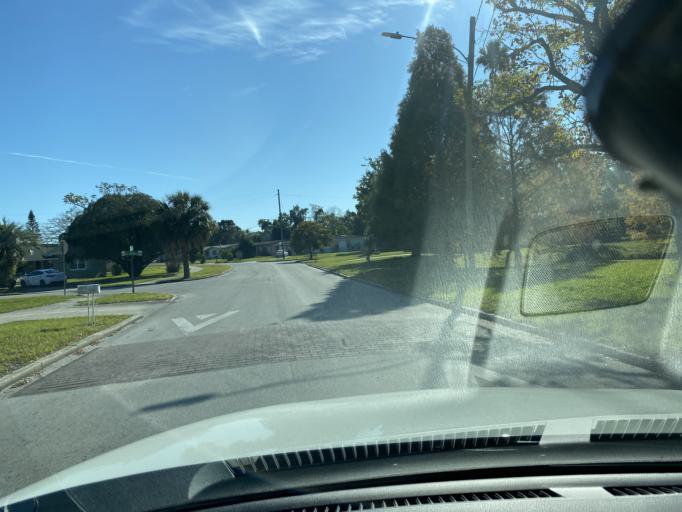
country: US
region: Florida
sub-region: Orange County
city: Azalea Park
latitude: 28.5271
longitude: -81.3170
